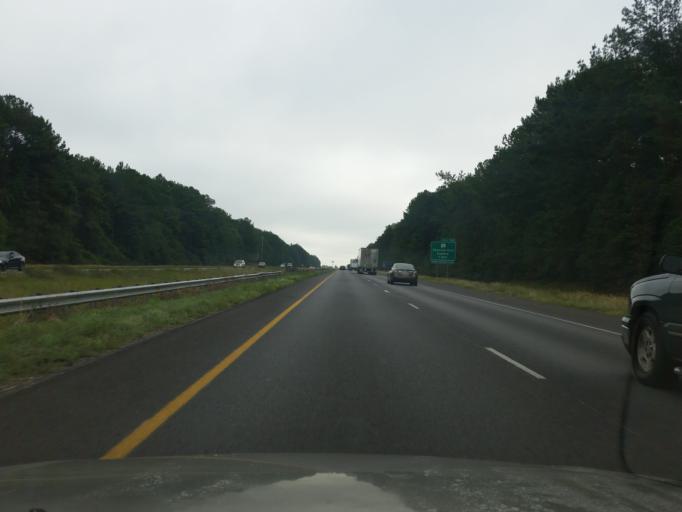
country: US
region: Alabama
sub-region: Baldwin County
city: Spanish Fort
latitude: 30.6609
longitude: -87.8722
